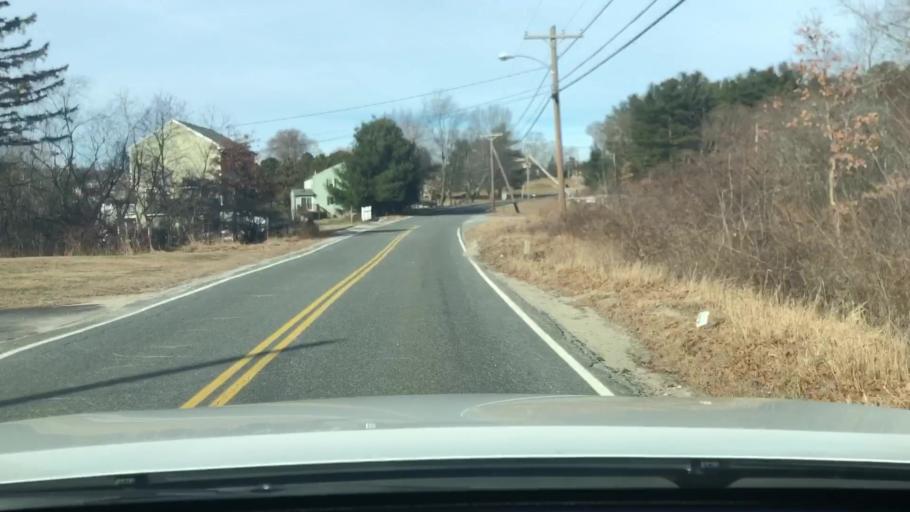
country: US
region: Massachusetts
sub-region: Worcester County
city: Blackstone
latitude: 42.0538
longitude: -71.5227
